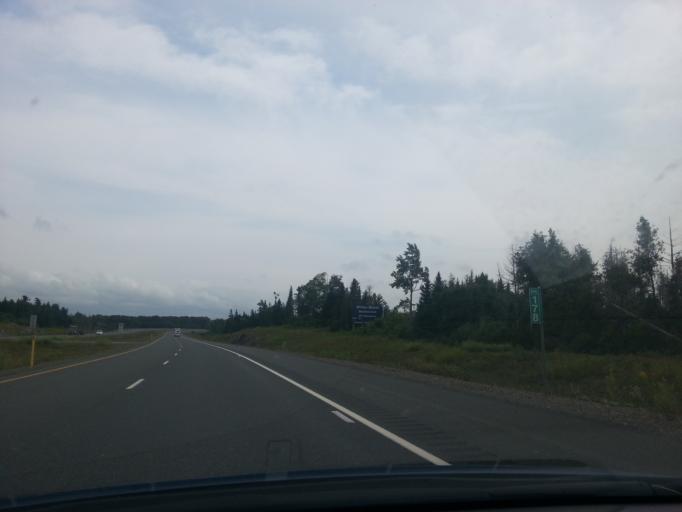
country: CA
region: New Brunswick
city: Florenceville-Bristol
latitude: 46.2420
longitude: -67.6012
